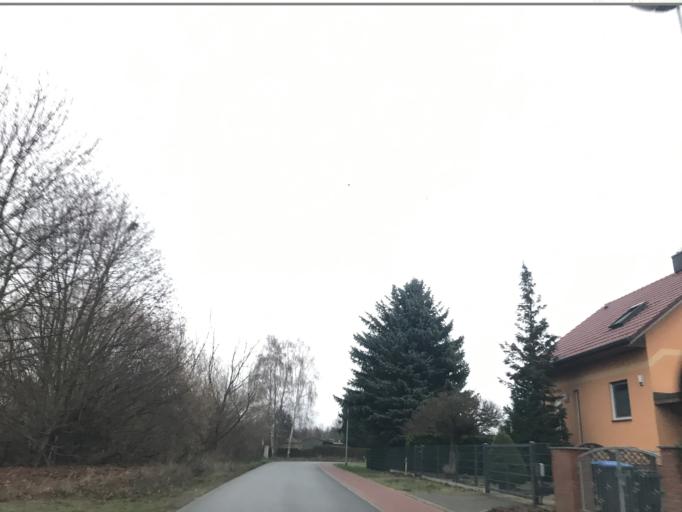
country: DE
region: Brandenburg
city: Falkensee
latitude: 52.5588
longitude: 13.1143
